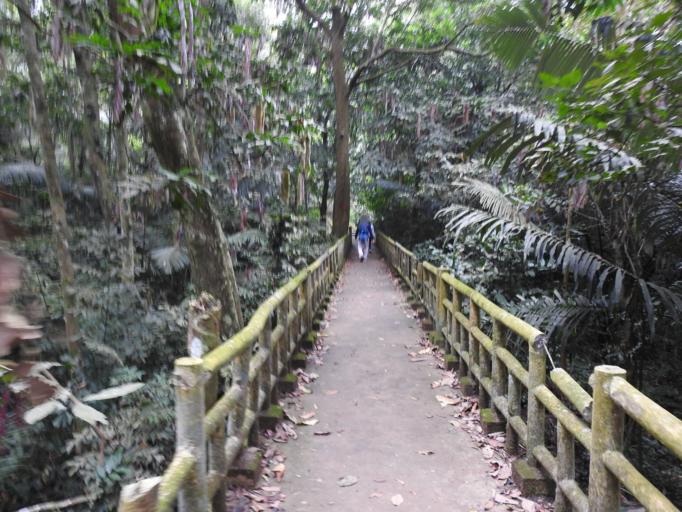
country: VN
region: Ninh Binh
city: Thi Tran Nho Quan
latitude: 20.2933
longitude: 105.6675
